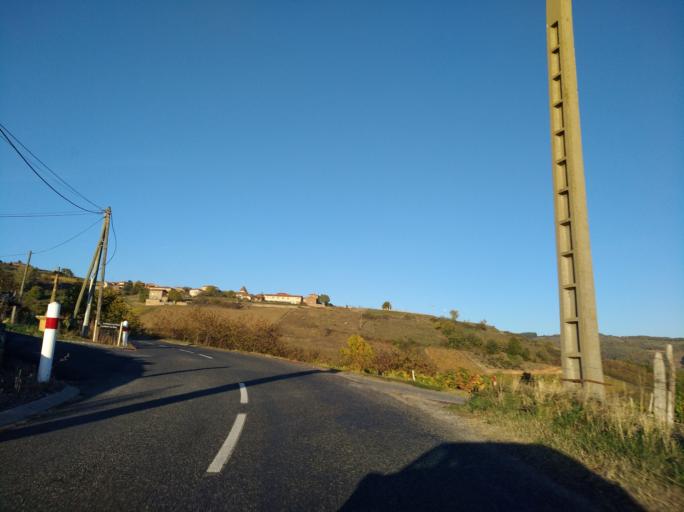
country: FR
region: Rhone-Alpes
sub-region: Departement du Rhone
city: Saint-Verand
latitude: 45.9570
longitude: 4.5620
